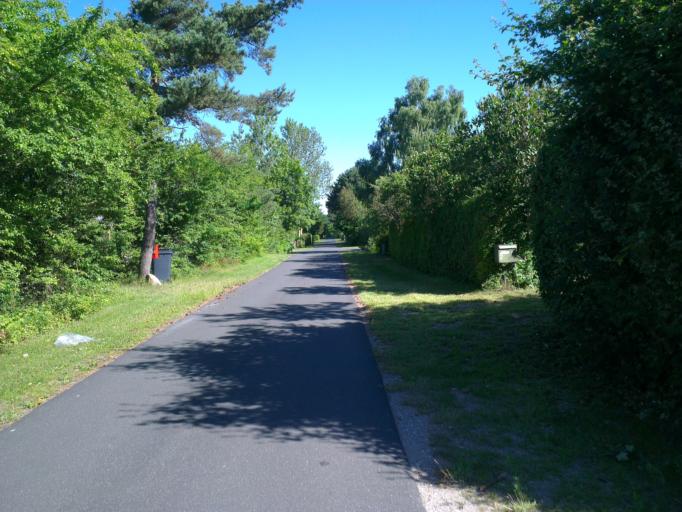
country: DK
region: Capital Region
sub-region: Halsnaes Kommune
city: Hundested
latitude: 55.9199
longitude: 11.9084
